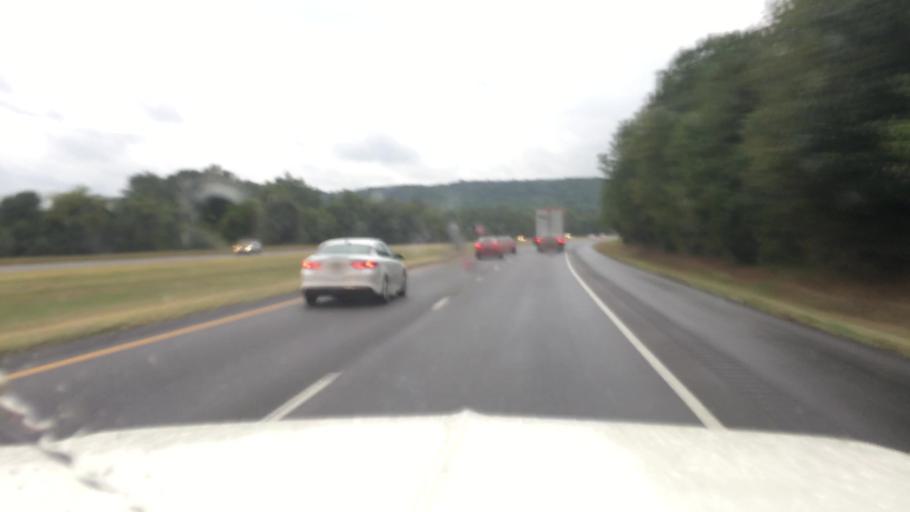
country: US
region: Alabama
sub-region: Morgan County
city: Falkville
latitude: 34.3454
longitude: -86.8925
